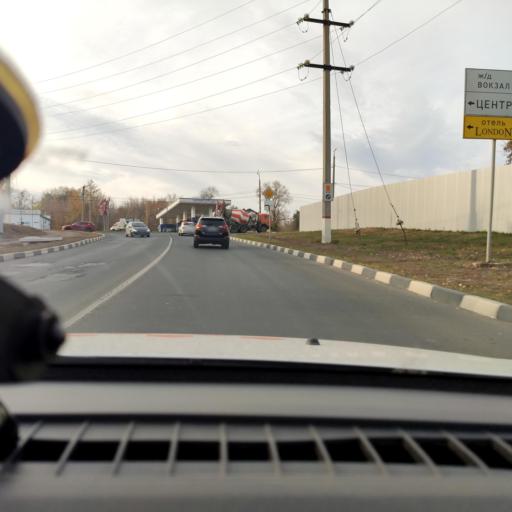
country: RU
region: Samara
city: Novokuybyshevsk
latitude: 53.1175
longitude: 49.9365
